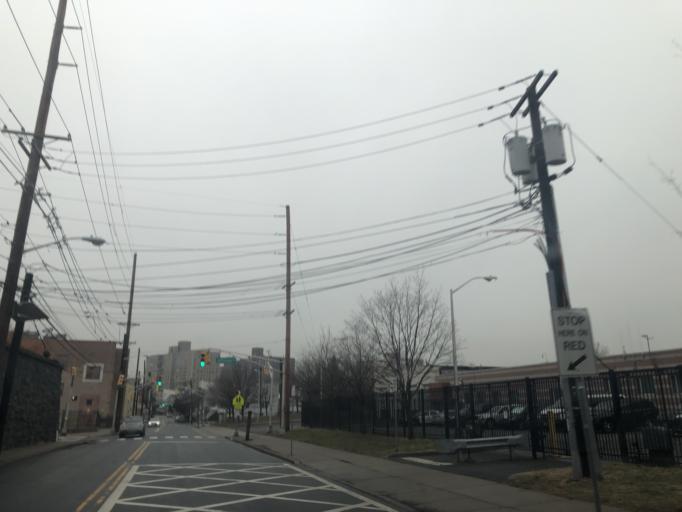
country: US
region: New Jersey
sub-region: Hudson County
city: Jersey City
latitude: 40.7404
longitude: -74.0565
